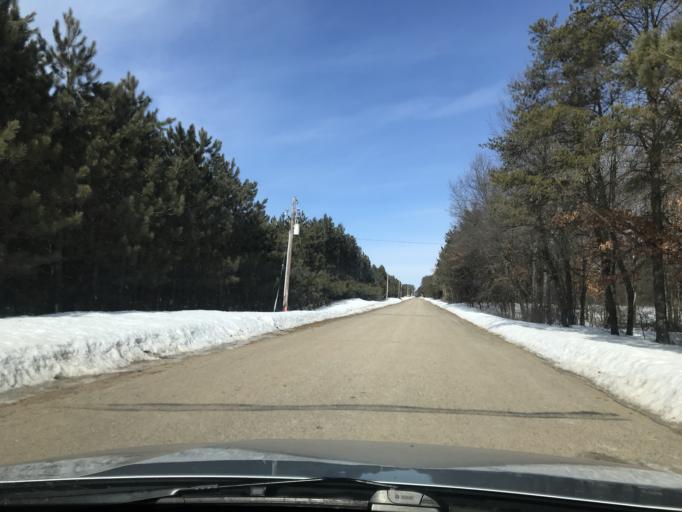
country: US
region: Wisconsin
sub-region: Marinette County
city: Peshtigo
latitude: 45.2133
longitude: -87.9626
